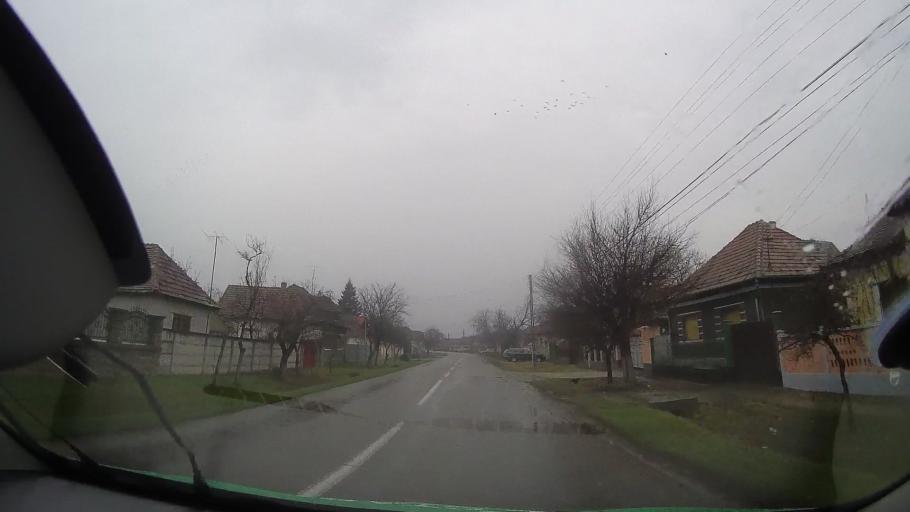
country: RO
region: Bihor
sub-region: Comuna Tulca
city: Tulca
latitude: 46.7914
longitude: 21.7710
